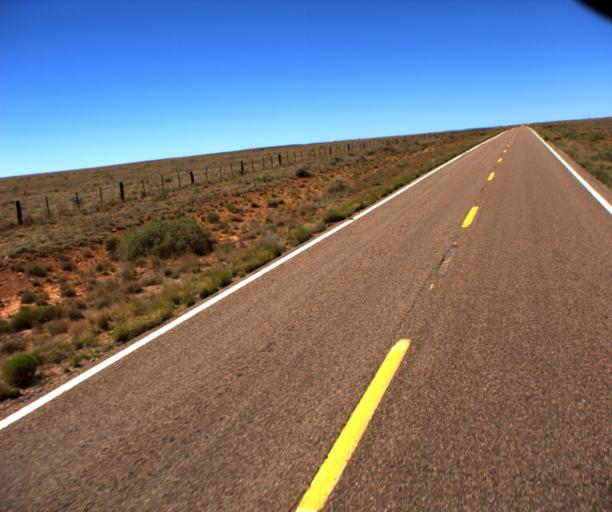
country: US
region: Arizona
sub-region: Navajo County
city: Winslow
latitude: 34.8855
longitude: -110.6501
